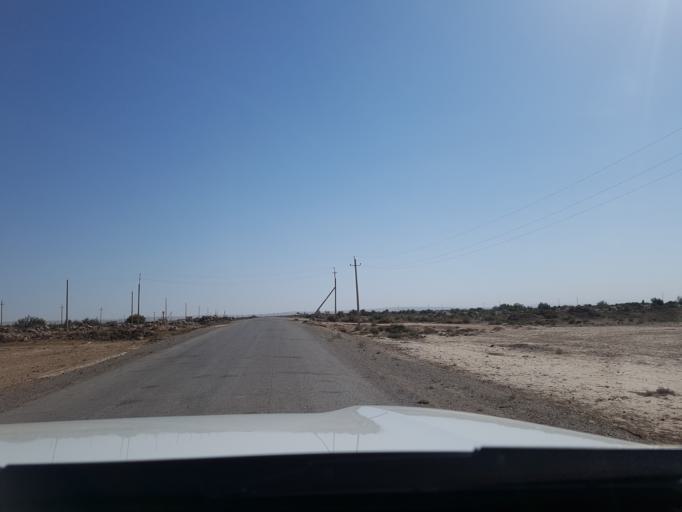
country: IR
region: Razavi Khorasan
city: Sarakhs
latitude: 36.4989
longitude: 61.2536
